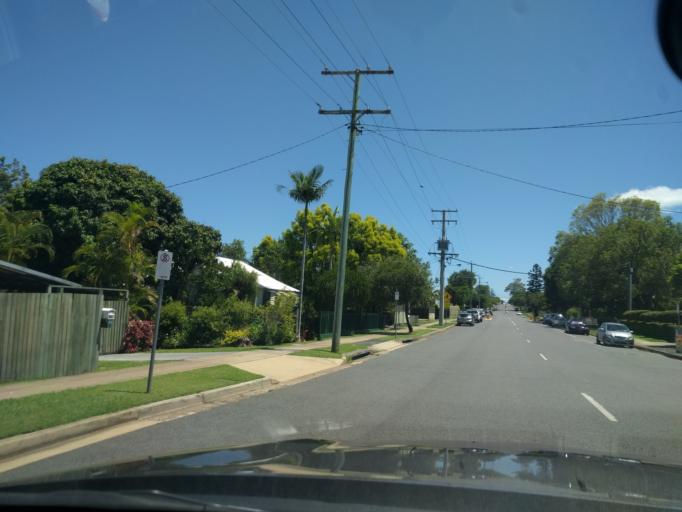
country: AU
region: Queensland
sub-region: Logan
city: Cedar Vale
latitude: -27.9898
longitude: 153.0020
